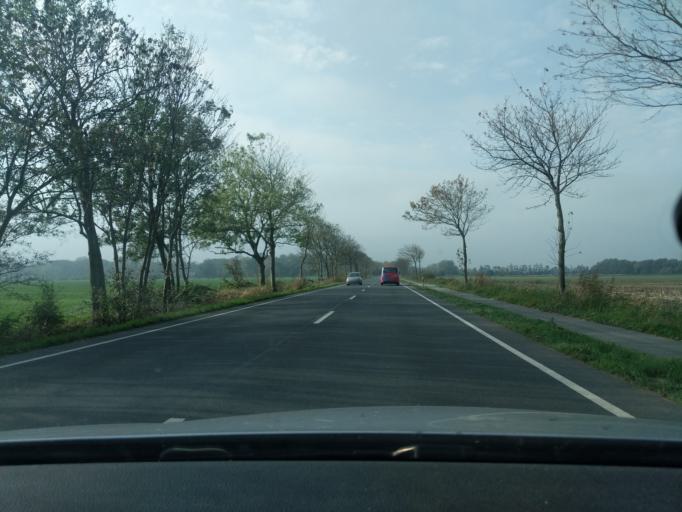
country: DE
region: Lower Saxony
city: Osterbruch
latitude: 53.8219
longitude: 8.9545
